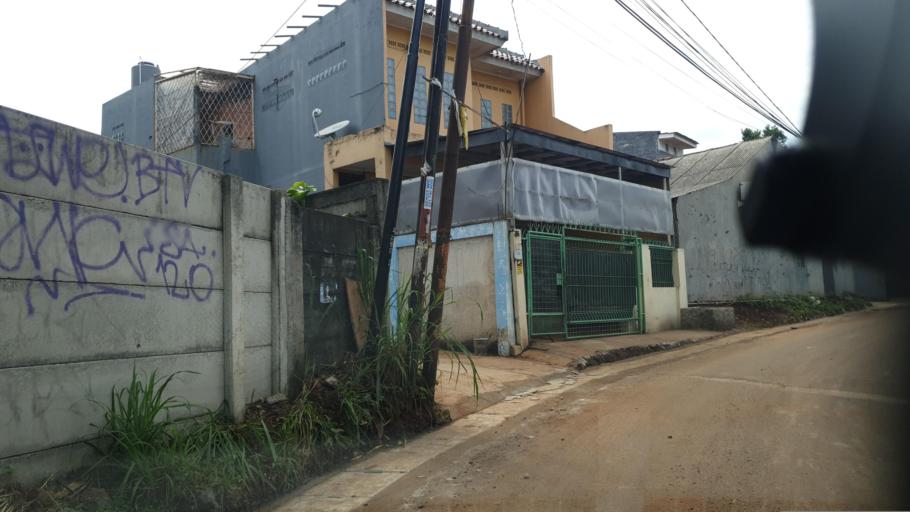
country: ID
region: West Java
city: Pamulang
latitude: -6.3460
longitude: 106.7666
